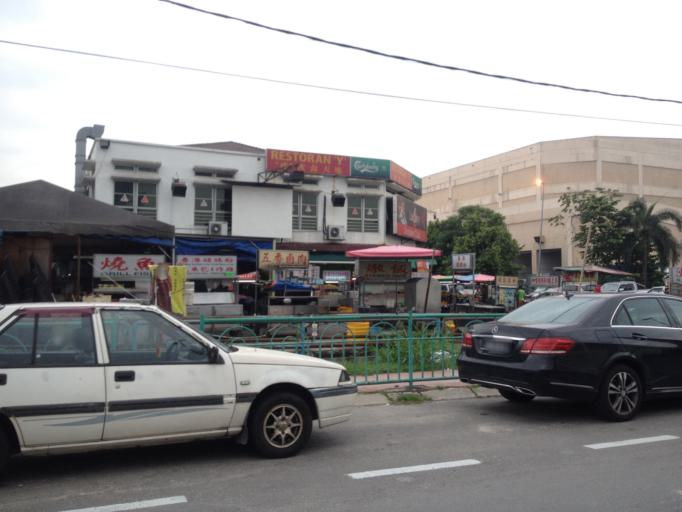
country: MY
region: Selangor
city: Kampong Baharu Balakong
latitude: 3.0332
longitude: 101.7629
